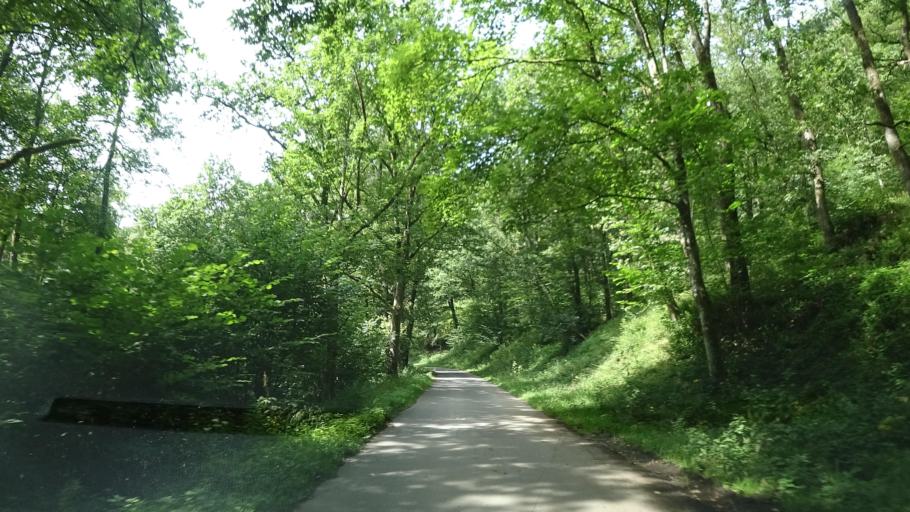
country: BE
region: Wallonia
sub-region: Province du Luxembourg
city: Herbeumont
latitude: 49.7771
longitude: 5.2572
